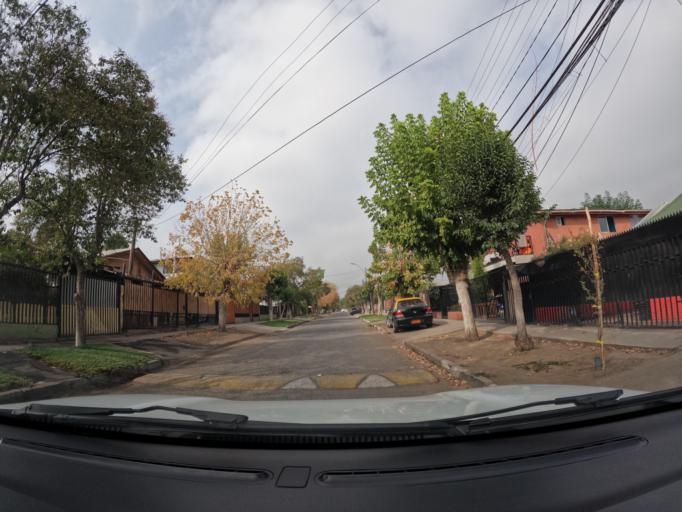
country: CL
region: Santiago Metropolitan
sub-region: Provincia de Santiago
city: Villa Presidente Frei, Nunoa, Santiago, Chile
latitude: -33.4714
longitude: -70.5461
